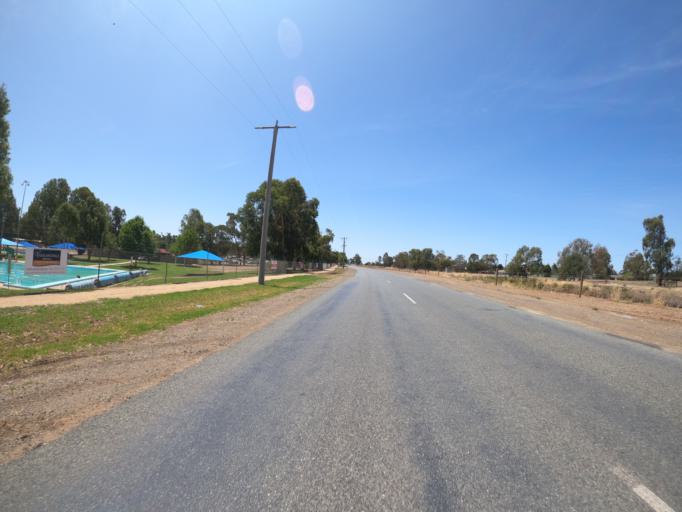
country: AU
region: Victoria
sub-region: Moira
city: Yarrawonga
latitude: -36.0141
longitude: 145.9973
